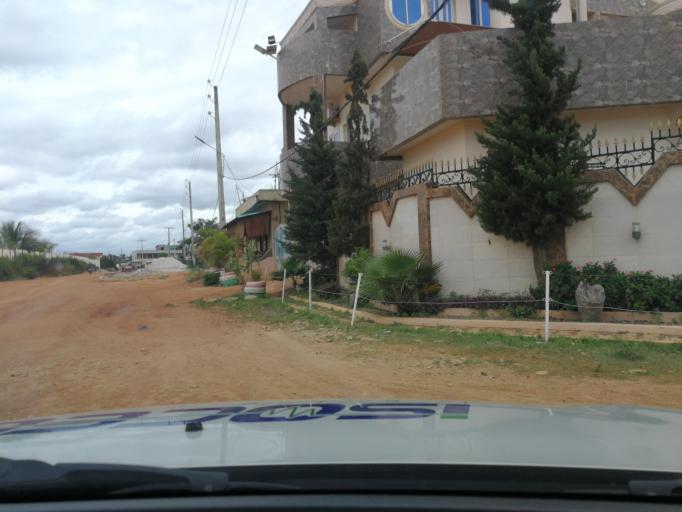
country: BJ
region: Atlantique
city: Abomey-Calavi
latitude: 6.4297
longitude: 2.3068
